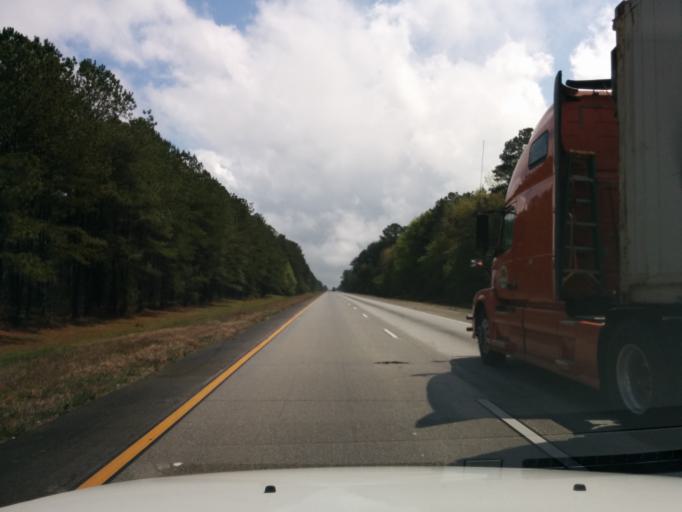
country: US
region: Georgia
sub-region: Candler County
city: Metter
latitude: 32.3439
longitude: -81.9651
